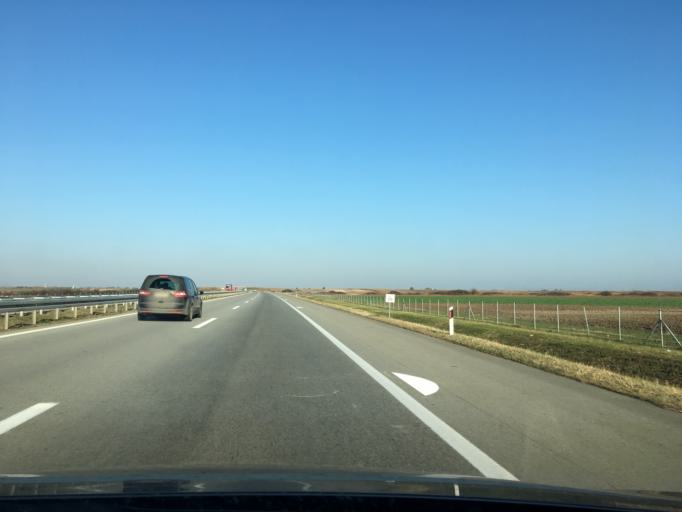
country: RS
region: Autonomna Pokrajina Vojvodina
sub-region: Juznobacki Okrug
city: Kovilj
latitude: 45.2196
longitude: 20.0613
